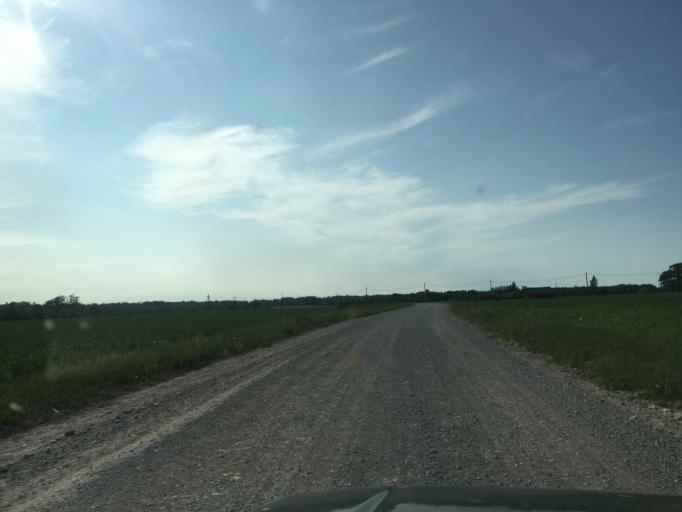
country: LV
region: Dundaga
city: Dundaga
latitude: 57.6220
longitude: 22.4105
